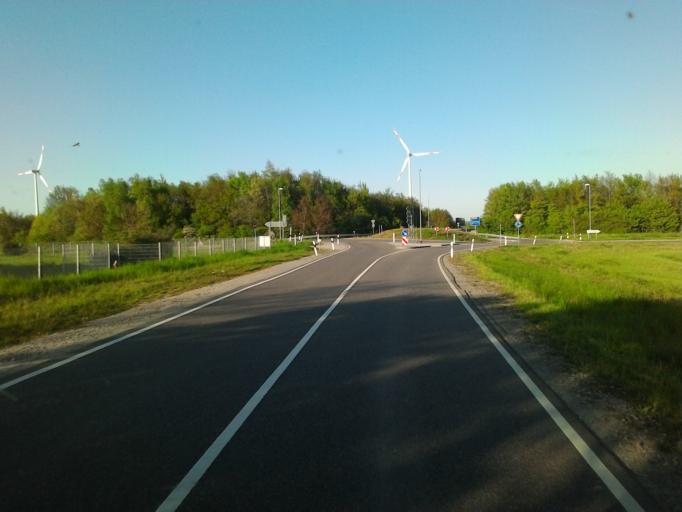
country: DE
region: Bavaria
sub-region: Regierungsbezirk Mittelfranken
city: Ohrenbach
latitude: 49.5106
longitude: 10.1950
